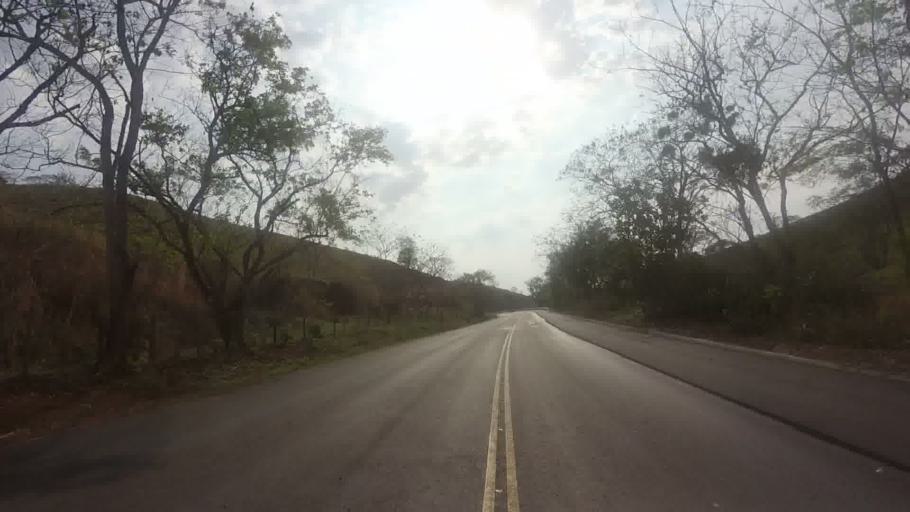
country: BR
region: Rio de Janeiro
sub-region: Itaperuna
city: Itaperuna
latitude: -21.2922
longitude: -41.8186
